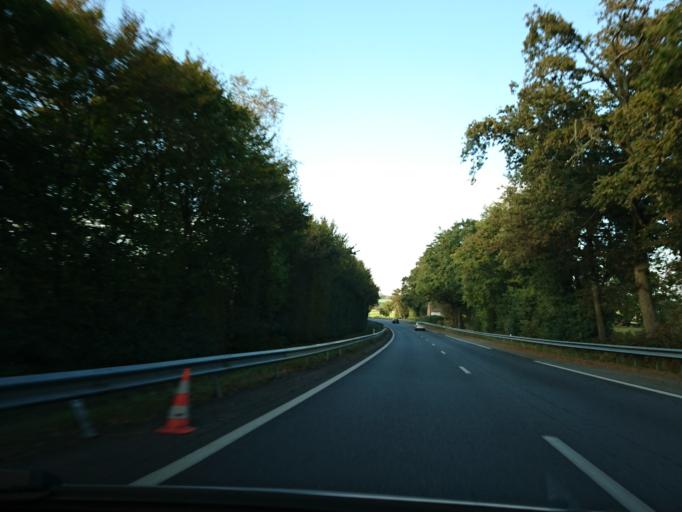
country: FR
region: Brittany
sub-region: Departement d'Ille-et-Vilaine
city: La Dominelais
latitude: 47.7980
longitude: -1.6900
